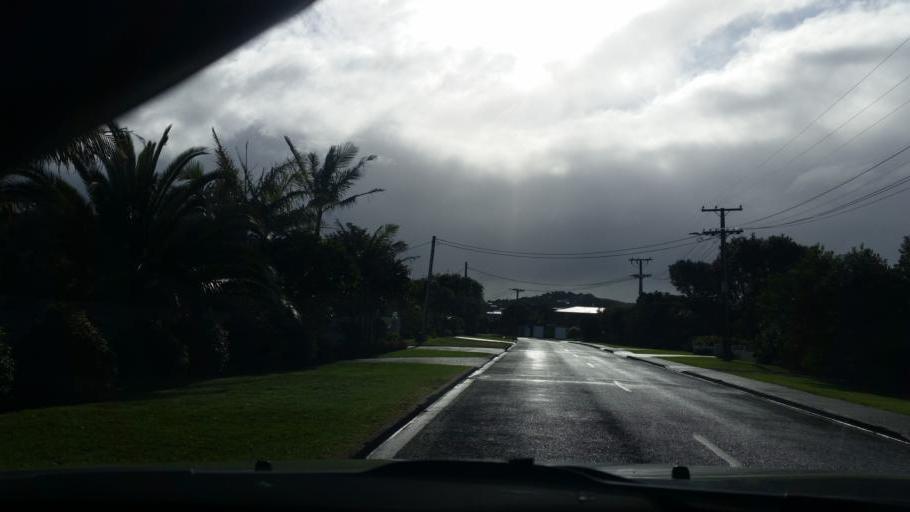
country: NZ
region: Auckland
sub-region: Auckland
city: Wellsford
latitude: -36.0932
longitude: 174.5905
